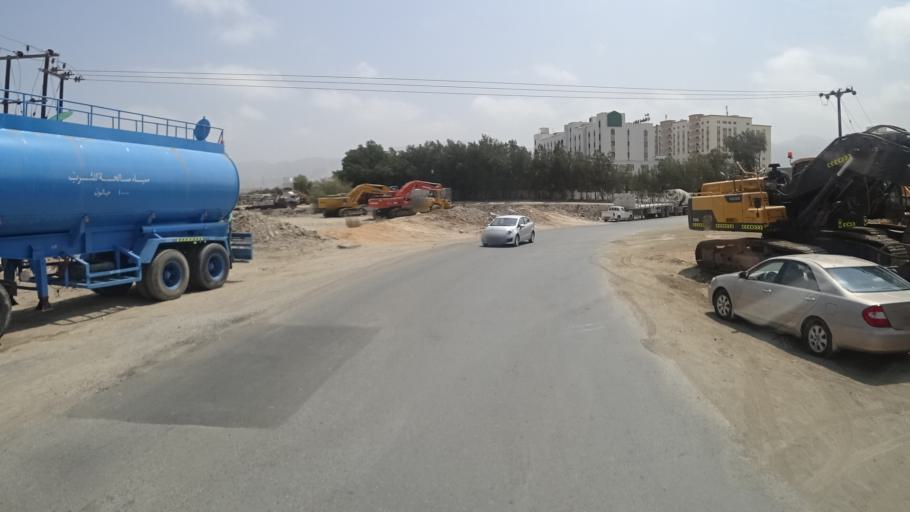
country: OM
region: Muhafazat Masqat
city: Bawshar
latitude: 23.5757
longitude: 58.3746
